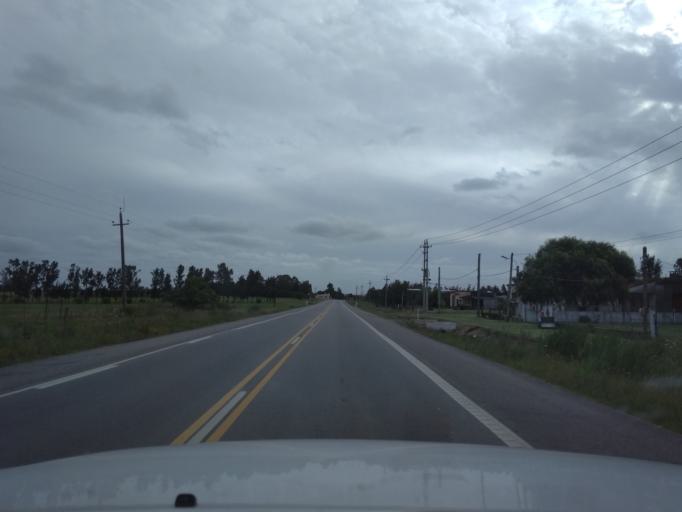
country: UY
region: Canelones
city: Joaquin Suarez
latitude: -34.7003
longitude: -56.0396
